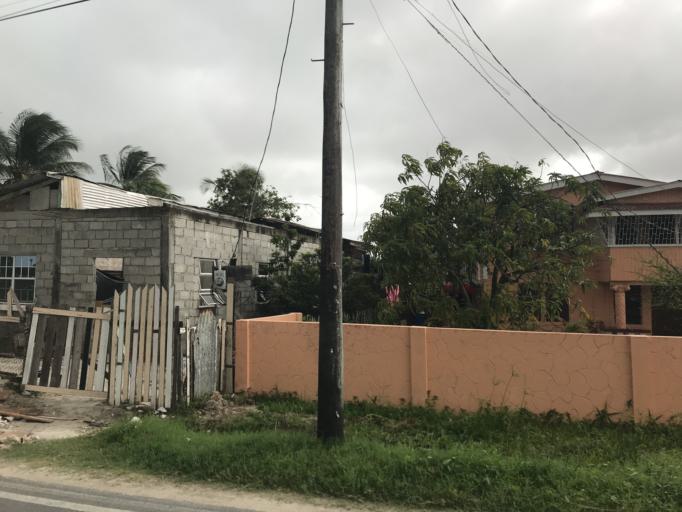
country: GY
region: Demerara-Mahaica
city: Georgetown
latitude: 6.8077
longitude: -58.1183
